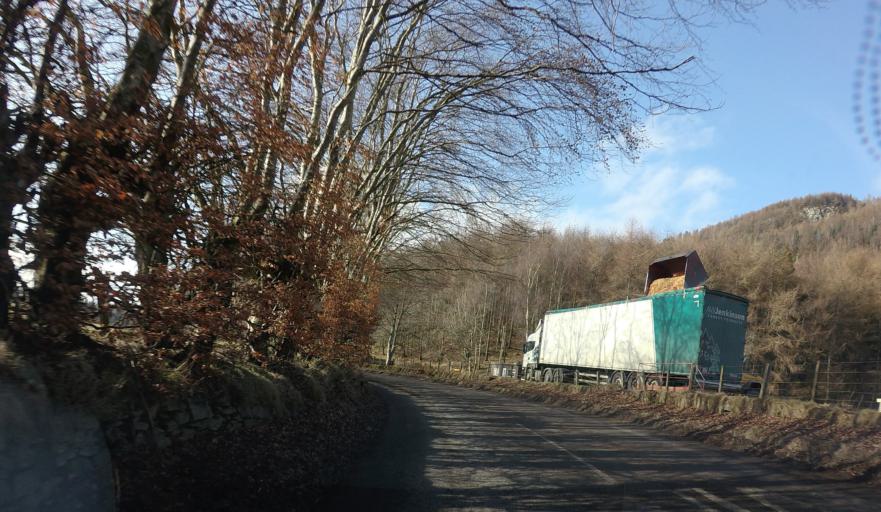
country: GB
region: Scotland
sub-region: Perth and Kinross
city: Bankfoot
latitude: 56.5715
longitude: -3.5984
